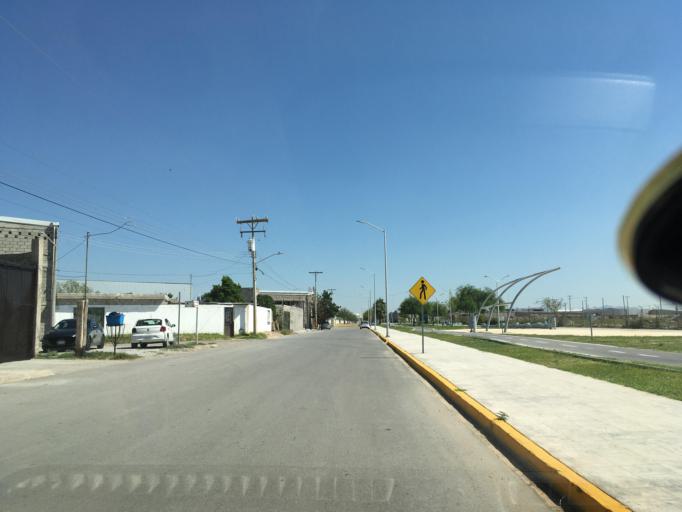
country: MX
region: Coahuila
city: Torreon
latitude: 25.5248
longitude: -103.3773
